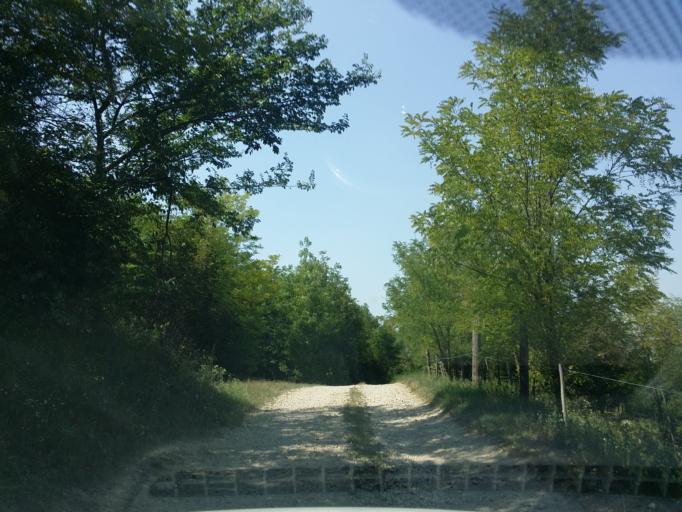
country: HU
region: Tolna
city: Gyonk
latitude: 46.5849
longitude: 18.4028
